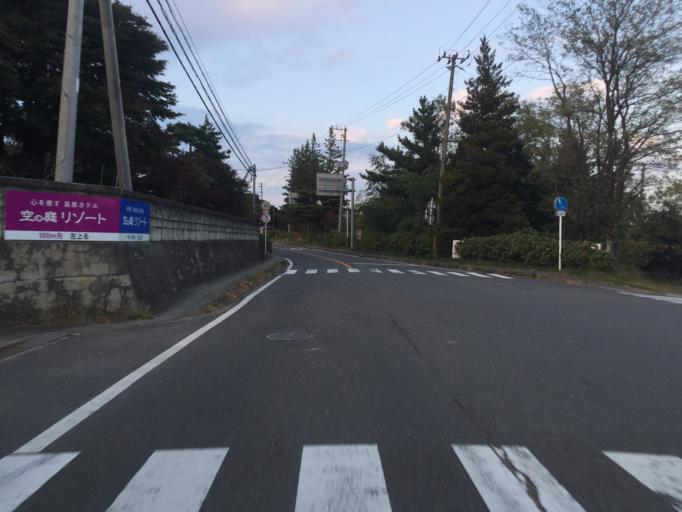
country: JP
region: Fukushima
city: Nihommatsu
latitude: 37.6031
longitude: 140.3562
